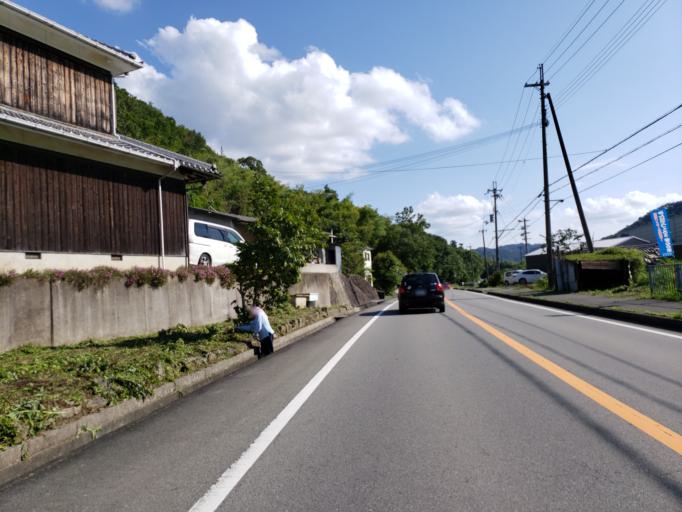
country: JP
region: Hyogo
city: Kakogawacho-honmachi
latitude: 34.8728
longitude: 134.7966
